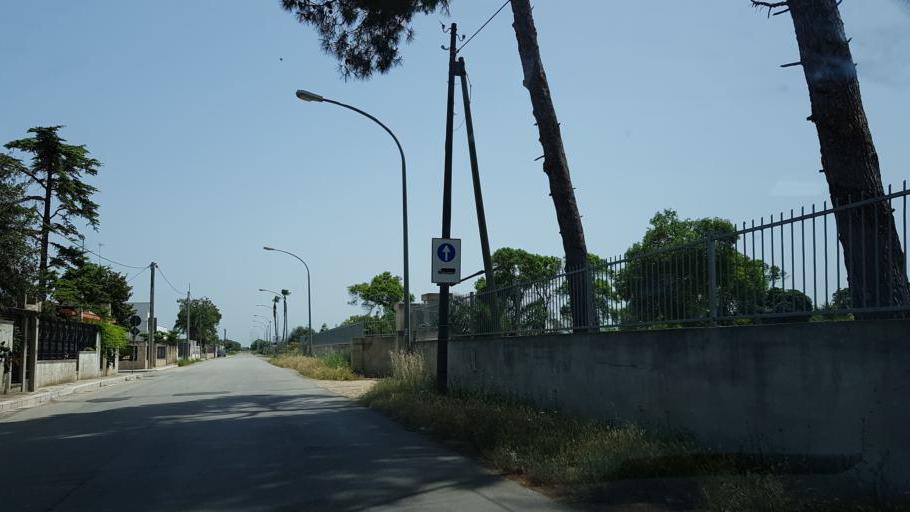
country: IT
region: Apulia
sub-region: Provincia di Brindisi
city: Mesagne
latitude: 40.5509
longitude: 17.8158
